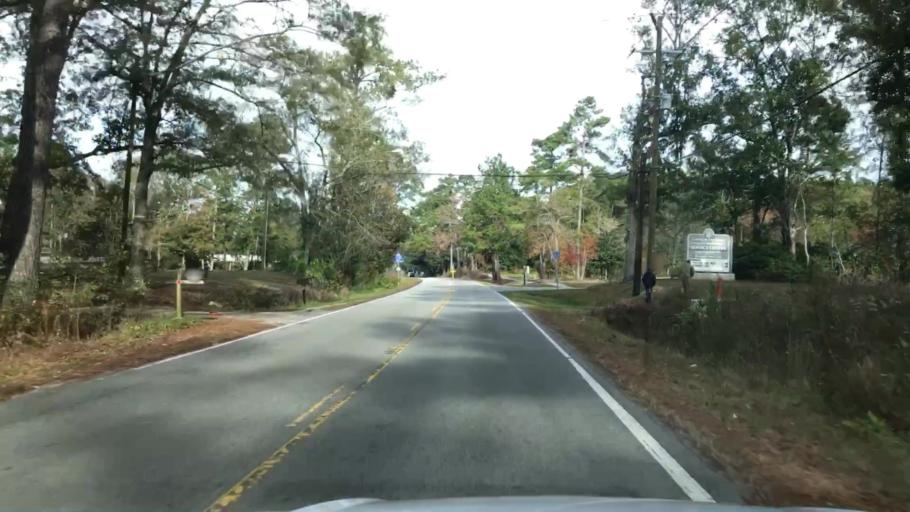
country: US
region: South Carolina
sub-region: Charleston County
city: Ravenel
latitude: 32.7733
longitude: -80.2449
